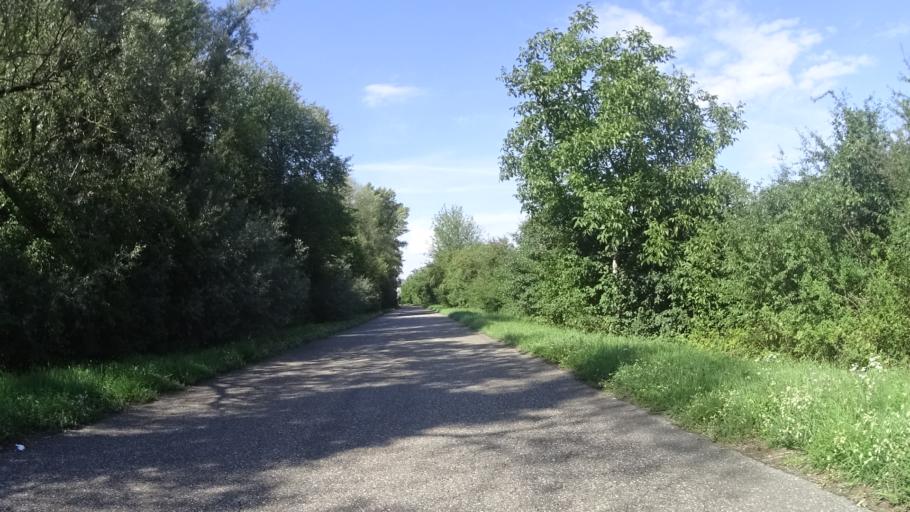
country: DE
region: Baden-Wuerttemberg
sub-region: Karlsruhe Region
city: Hugelsheim
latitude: 48.8212
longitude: 8.1007
